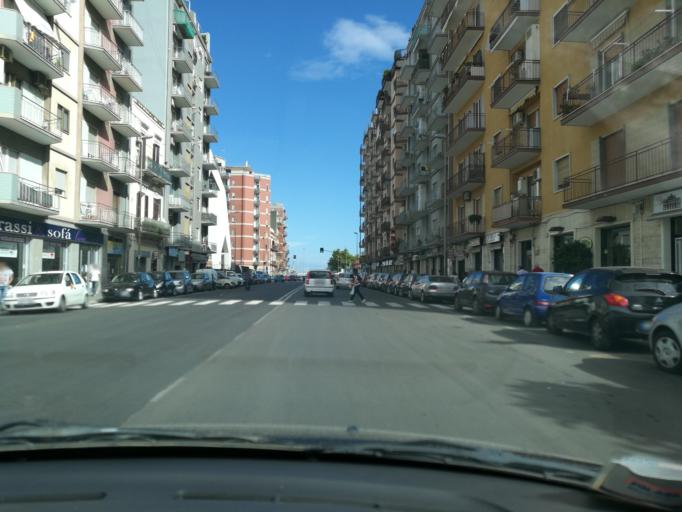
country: IT
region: Apulia
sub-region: Provincia di Bari
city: Bari
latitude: 41.1260
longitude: 16.8518
